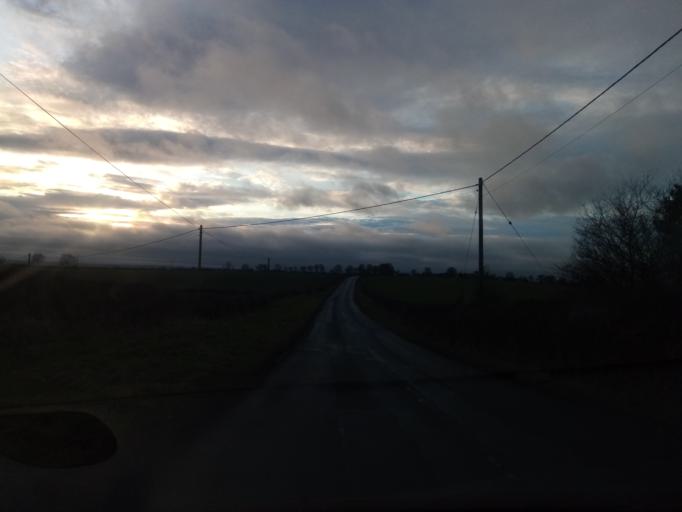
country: GB
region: England
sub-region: Northumberland
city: Meldon
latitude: 55.1353
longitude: -1.7620
